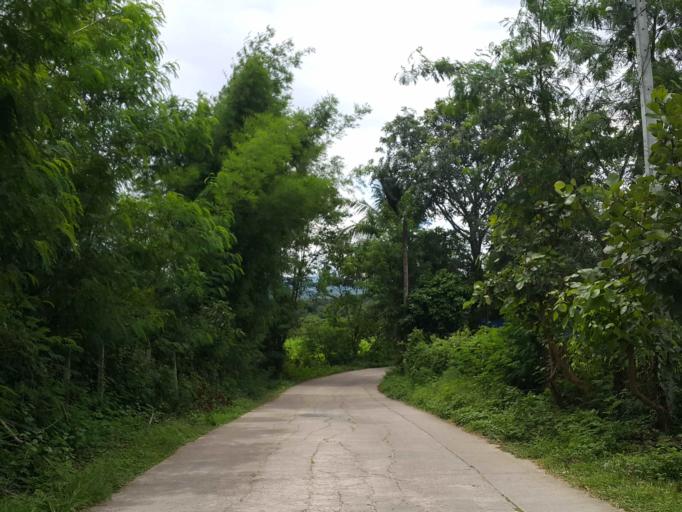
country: TH
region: Chiang Mai
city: San Sai
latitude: 18.9280
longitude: 98.9212
